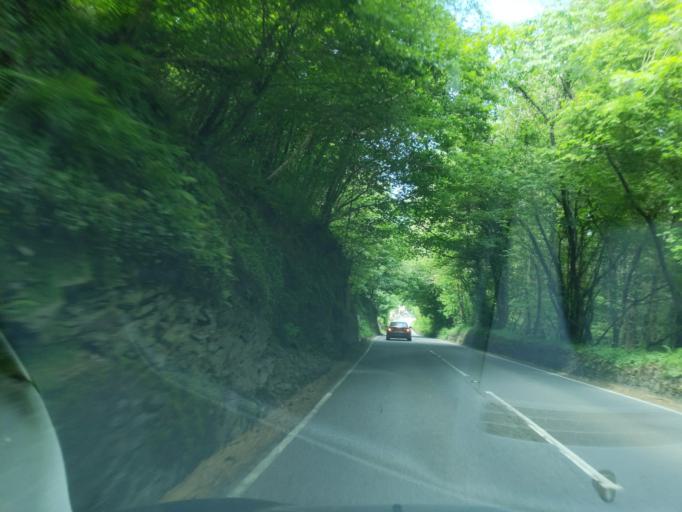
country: GB
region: England
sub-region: Cornwall
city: South Hill
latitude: 50.5669
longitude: -4.3348
